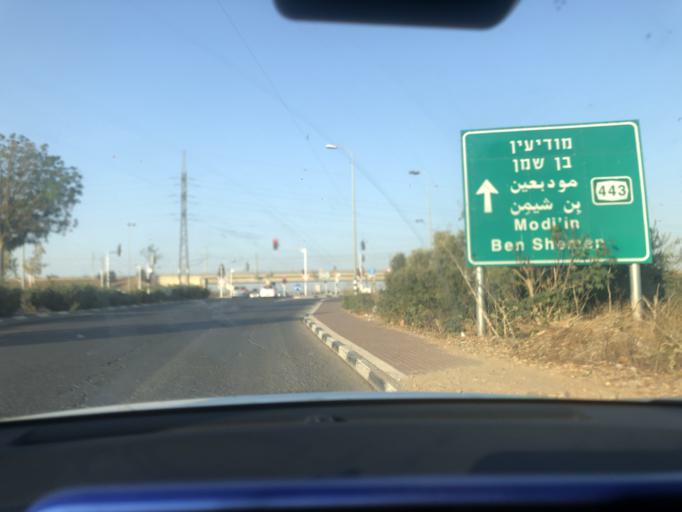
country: IL
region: Central District
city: Lod
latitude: 31.9563
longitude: 34.9059
